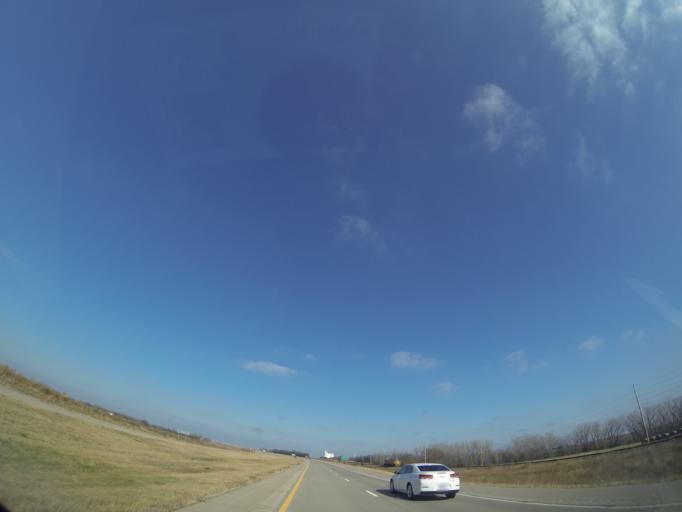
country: US
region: Kansas
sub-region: McPherson County
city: Inman
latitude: 38.2178
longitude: -97.7889
